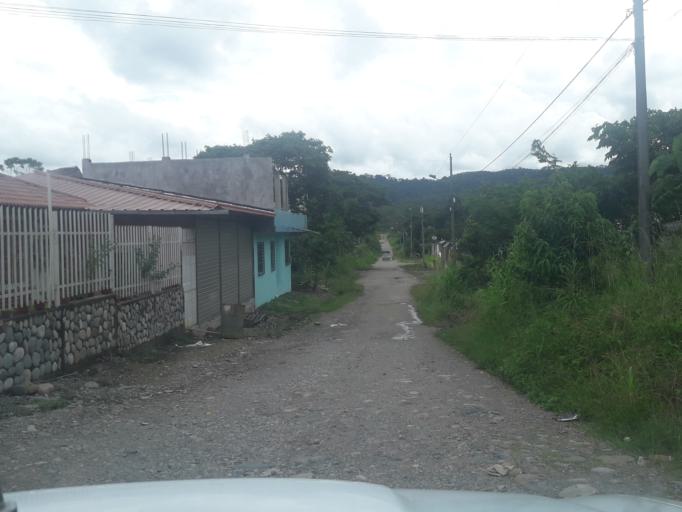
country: EC
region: Napo
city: Archidona
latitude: -0.9507
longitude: -77.8126
